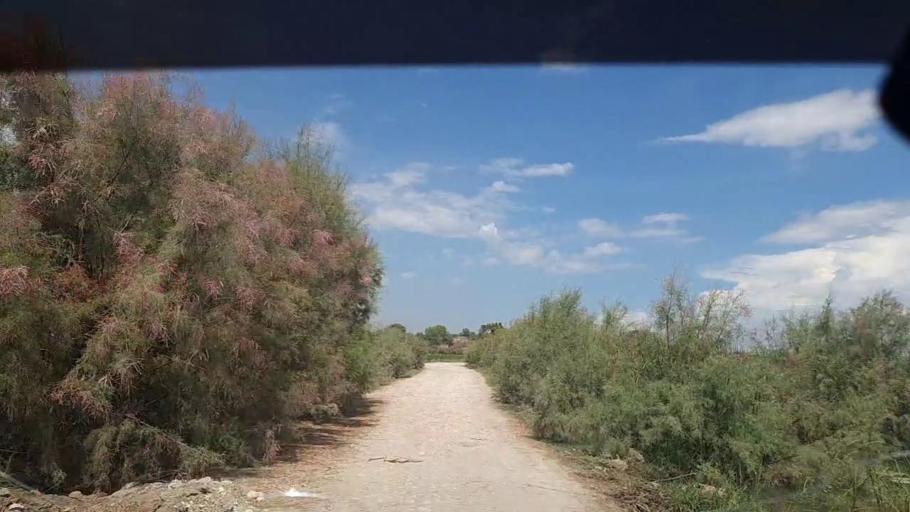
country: PK
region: Sindh
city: Ghauspur
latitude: 28.1436
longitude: 68.9803
